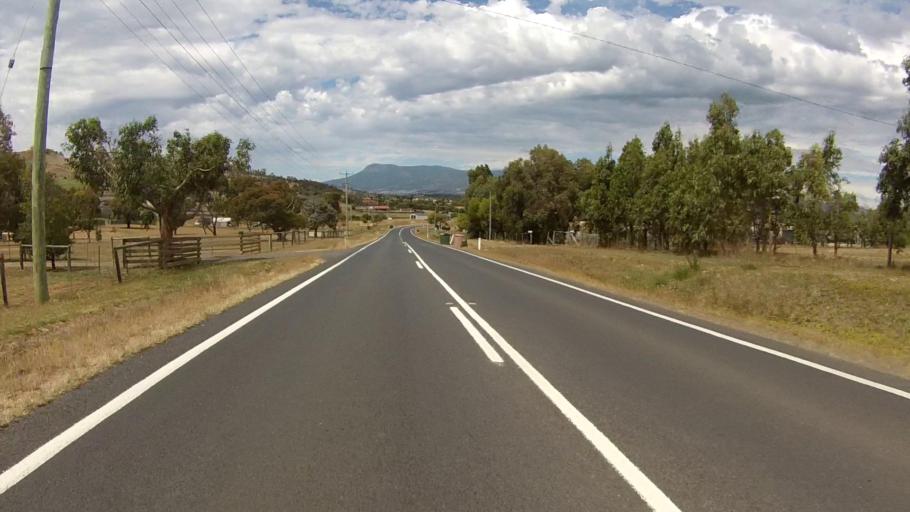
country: AU
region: Tasmania
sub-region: Brighton
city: Bridgewater
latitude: -42.6976
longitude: 147.2694
